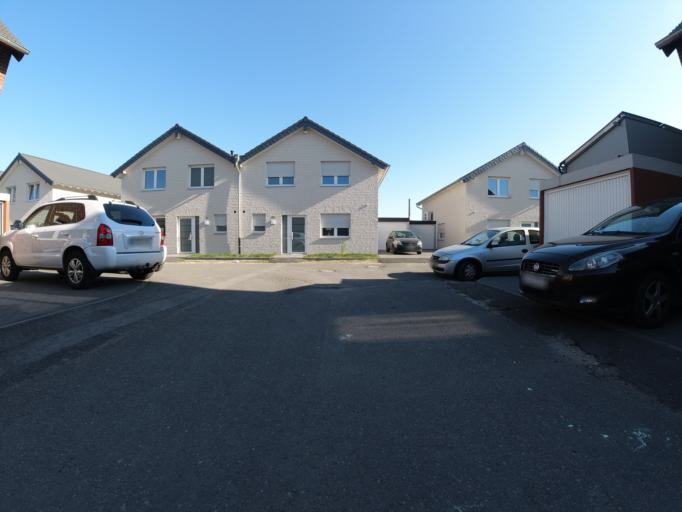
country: DE
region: North Rhine-Westphalia
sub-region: Regierungsbezirk Dusseldorf
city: Hochfeld
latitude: 51.3836
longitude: 6.7109
